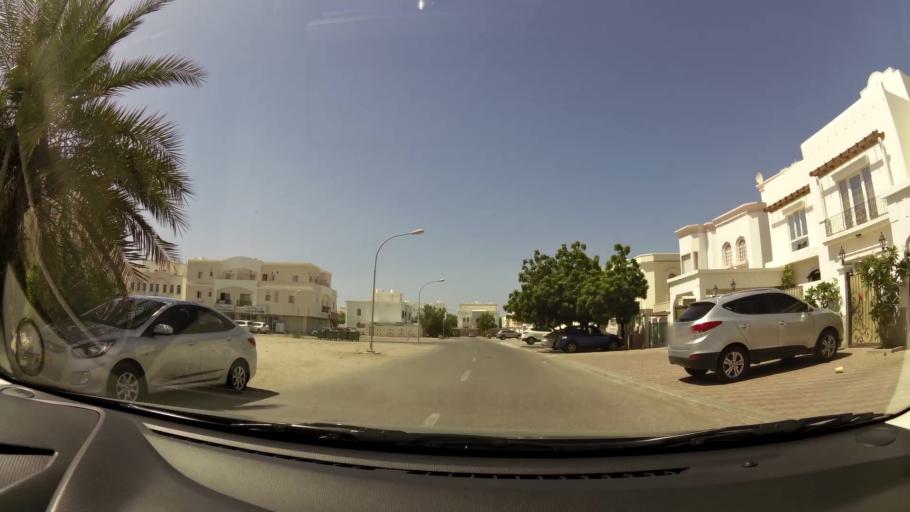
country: OM
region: Muhafazat Masqat
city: Bawshar
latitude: 23.5978
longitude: 58.3601
